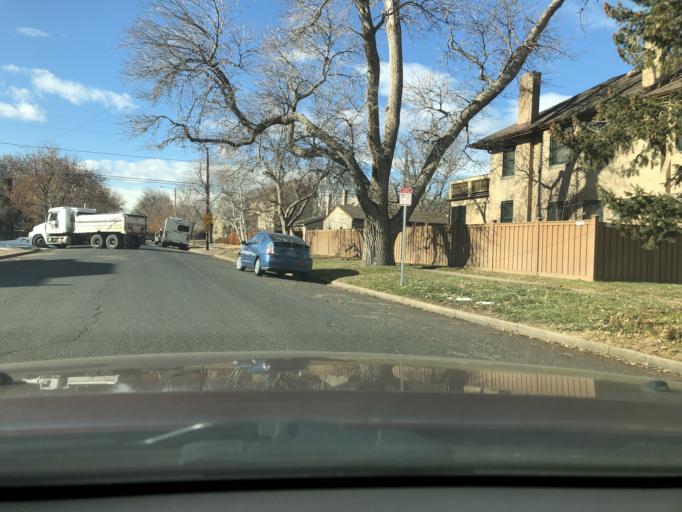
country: US
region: Colorado
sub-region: Denver County
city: Denver
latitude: 39.7558
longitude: -104.9623
